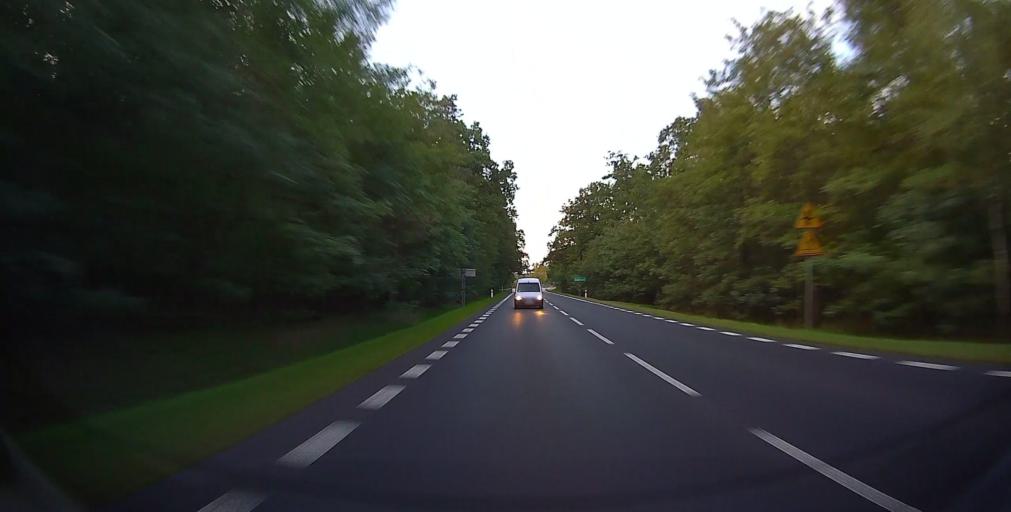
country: PL
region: Masovian Voivodeship
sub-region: Powiat kozienicki
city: Ryczywol
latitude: 51.7068
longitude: 21.4027
